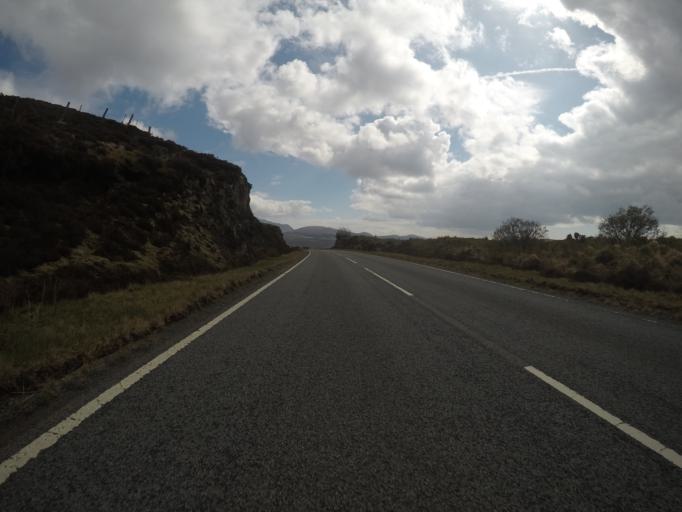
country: GB
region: Scotland
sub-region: Highland
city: Isle of Skye
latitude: 57.3121
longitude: -6.3192
